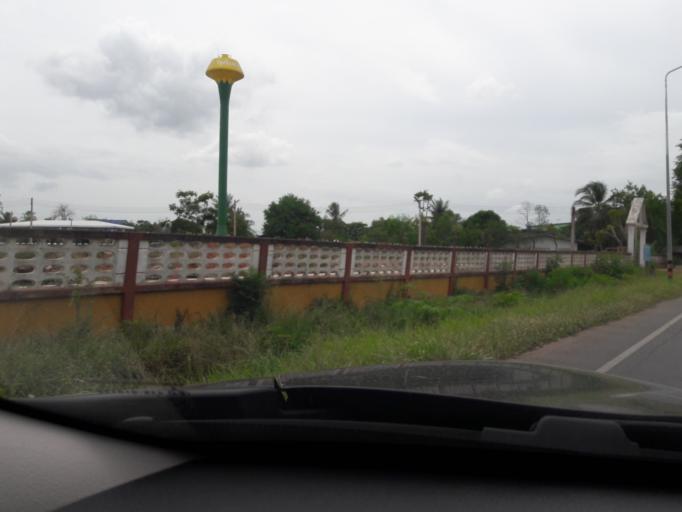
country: TH
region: Ratchaburi
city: Damnoen Saduak
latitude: 13.5928
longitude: 99.9396
